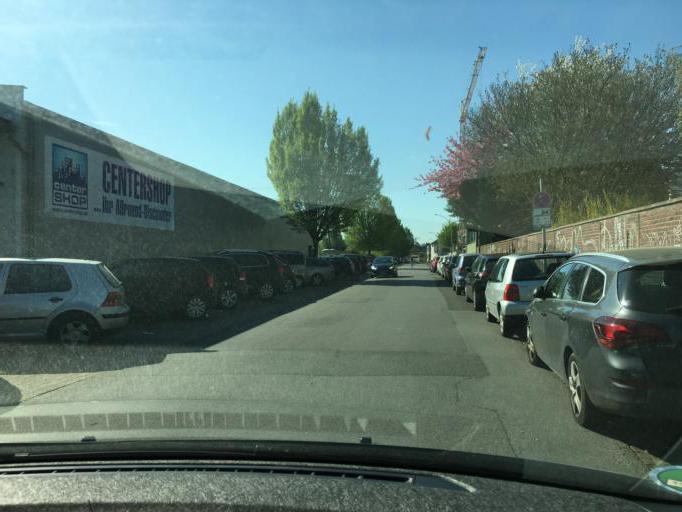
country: DE
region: North Rhine-Westphalia
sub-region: Regierungsbezirk Dusseldorf
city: Monchengladbach
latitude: 51.1622
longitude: 6.4386
